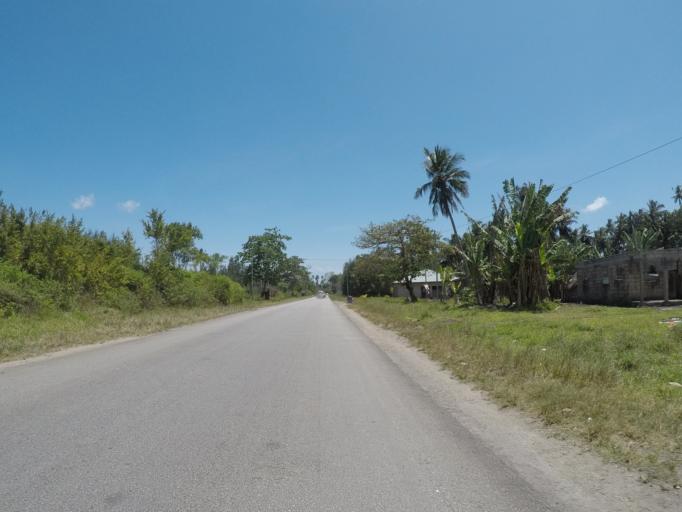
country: TZ
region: Zanzibar Central/South
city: Nganane
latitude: -6.2706
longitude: 39.4241
